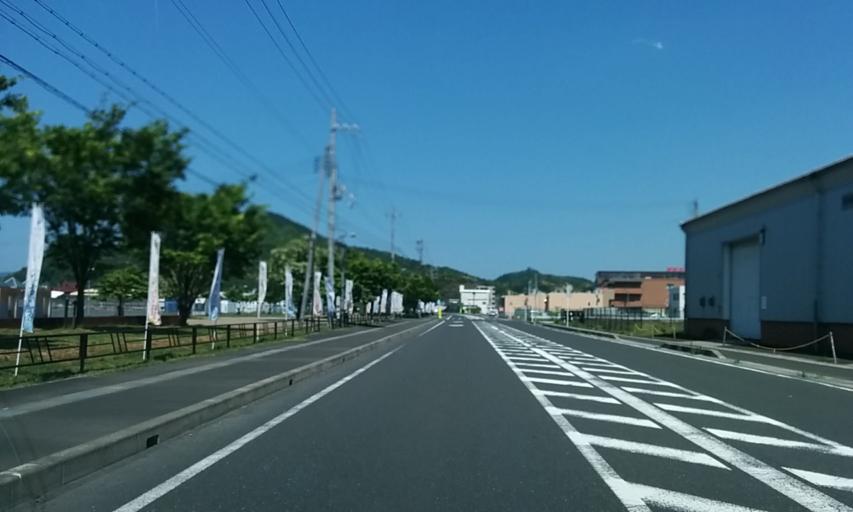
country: JP
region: Kyoto
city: Maizuru
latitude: 35.4511
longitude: 135.3184
